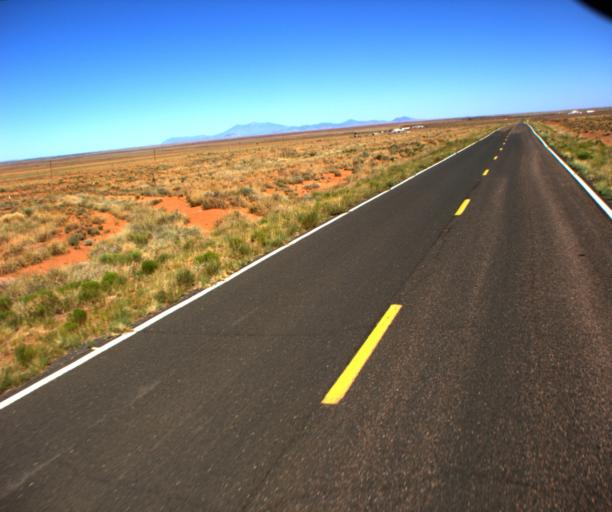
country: US
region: Arizona
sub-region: Coconino County
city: LeChee
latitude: 35.1300
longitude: -110.8788
